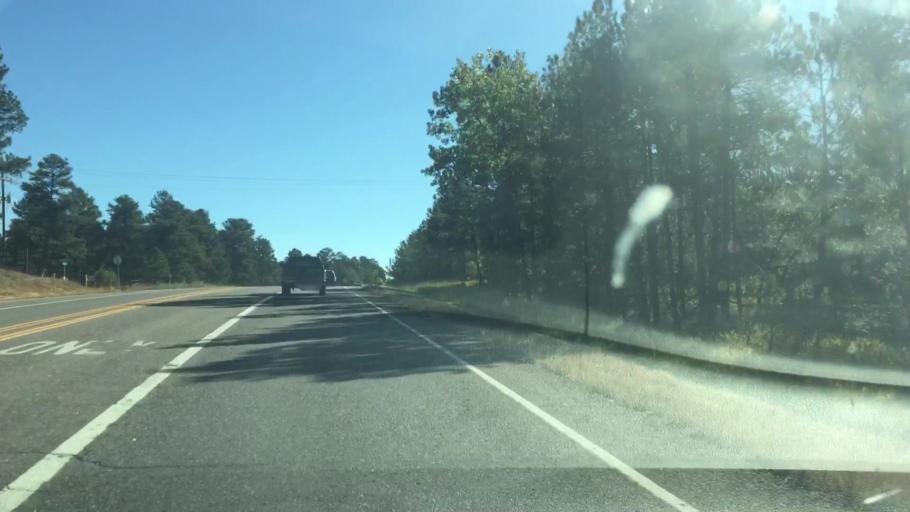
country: US
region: Colorado
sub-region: Elbert County
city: Elizabeth
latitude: 39.3617
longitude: -104.5793
